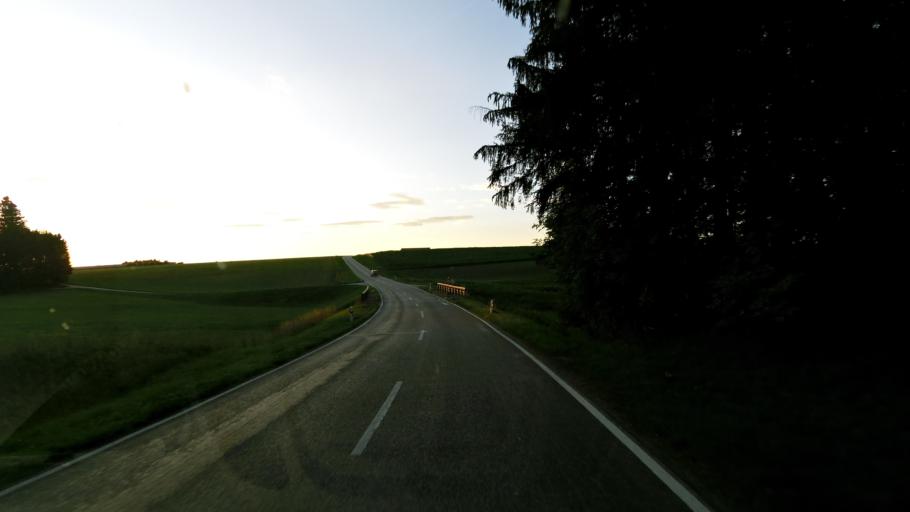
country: DE
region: Bavaria
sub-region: Upper Bavaria
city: Kienberg
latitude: 48.0982
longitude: 12.4777
